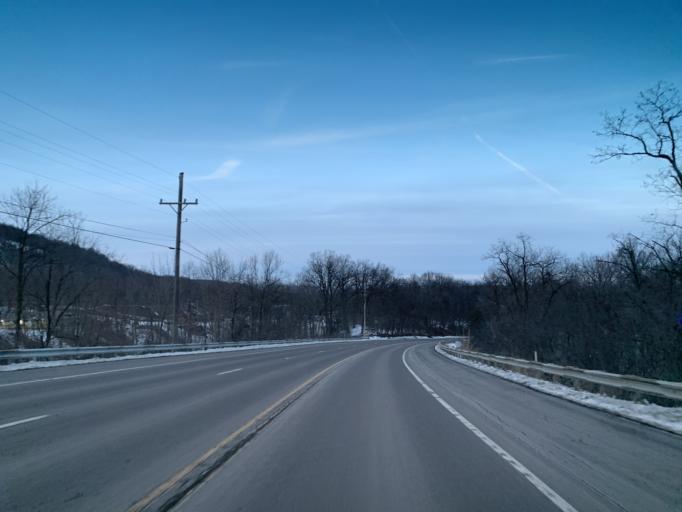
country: US
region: Maryland
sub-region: Allegany County
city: Cumberland
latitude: 39.7098
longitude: -78.6152
